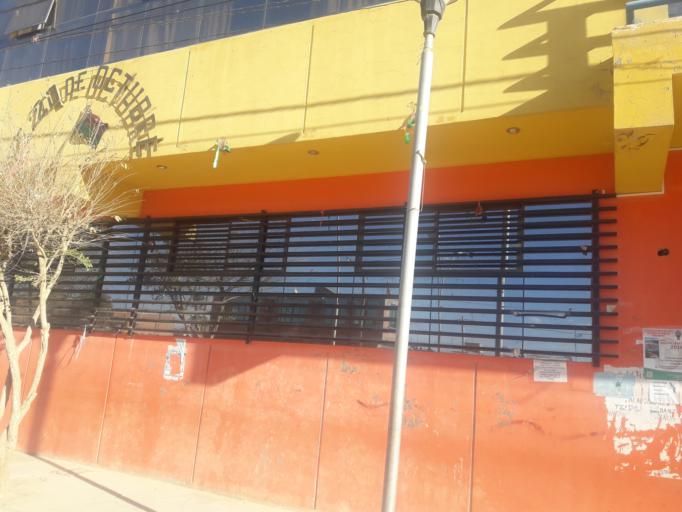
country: BO
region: La Paz
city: La Paz
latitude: -16.6494
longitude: -68.2986
